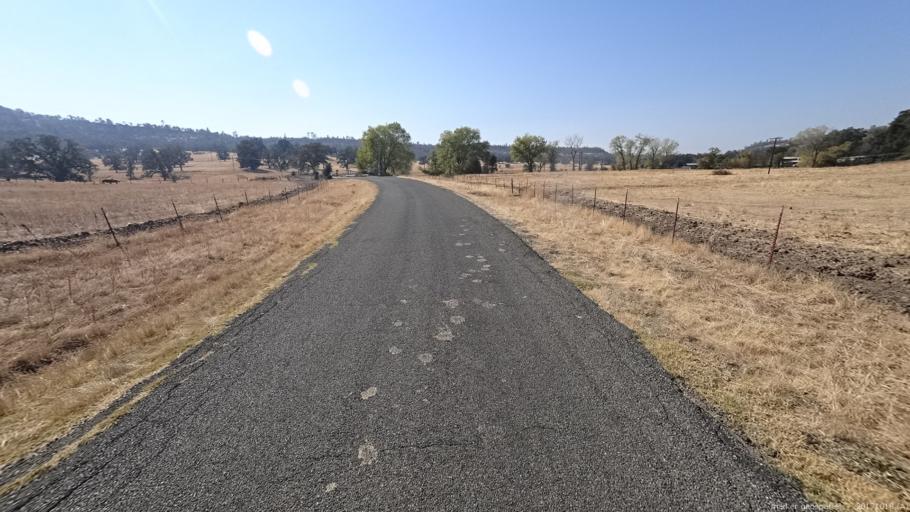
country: US
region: California
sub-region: Shasta County
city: Palo Cedro
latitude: 40.5491
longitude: -122.0767
